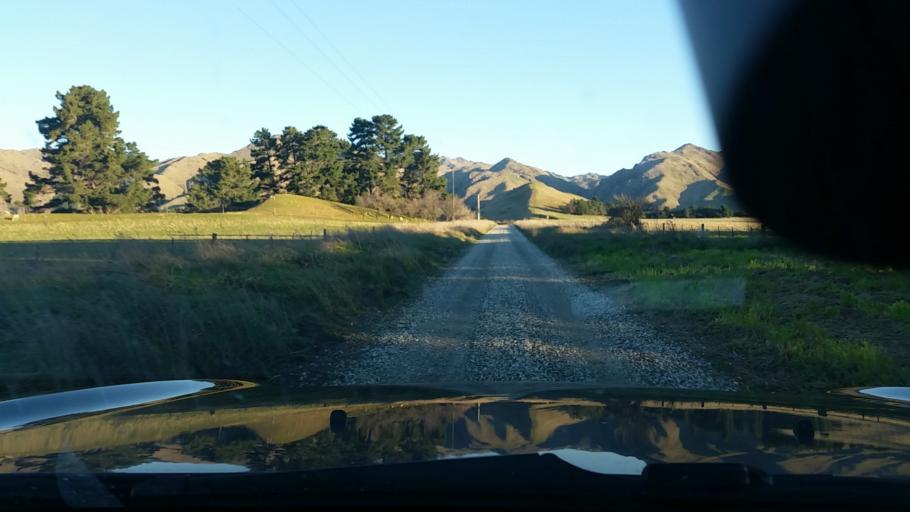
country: NZ
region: Marlborough
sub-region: Marlborough District
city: Blenheim
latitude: -41.7262
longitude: 174.0380
